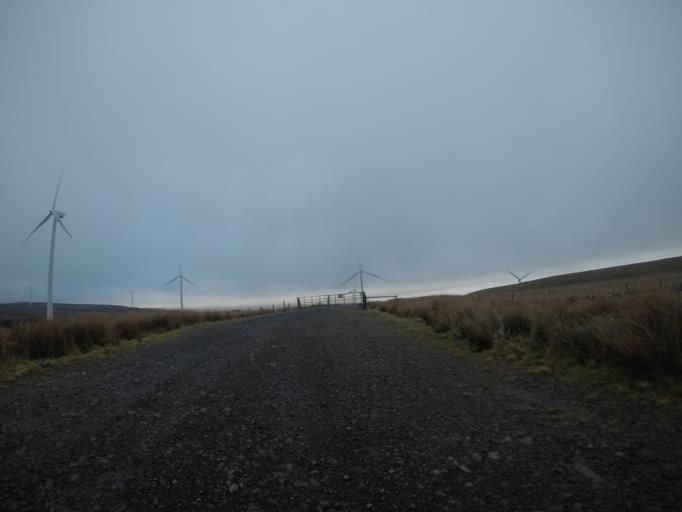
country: GB
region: Scotland
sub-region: North Ayrshire
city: Dalry
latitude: 55.7372
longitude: -4.7826
